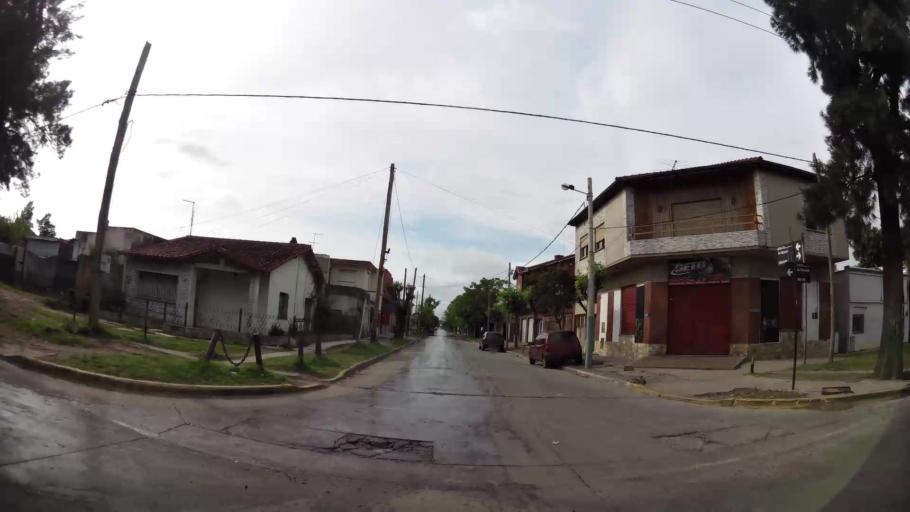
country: AR
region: Buenos Aires
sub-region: Partido de Quilmes
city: Quilmes
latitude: -34.7151
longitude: -58.2445
